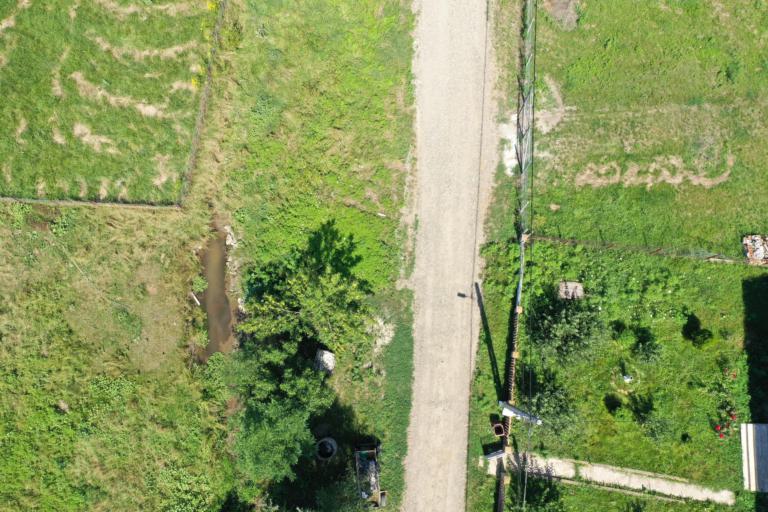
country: RO
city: Vanatori
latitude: 47.2525
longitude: 27.5220
